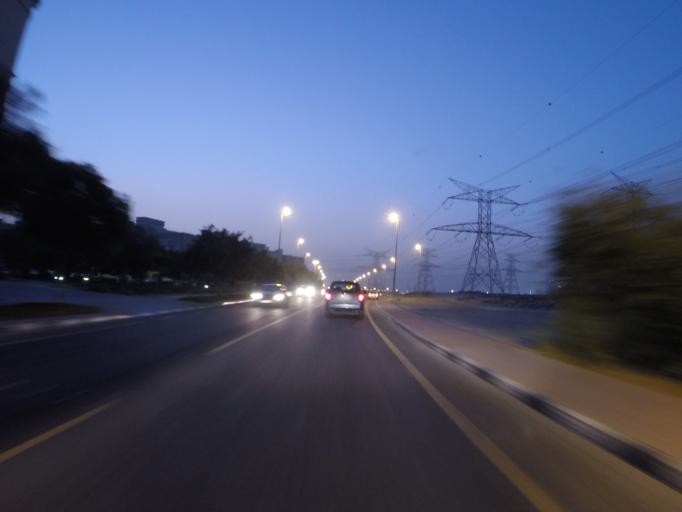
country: AE
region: Dubai
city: Dubai
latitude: 25.0482
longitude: 55.1374
